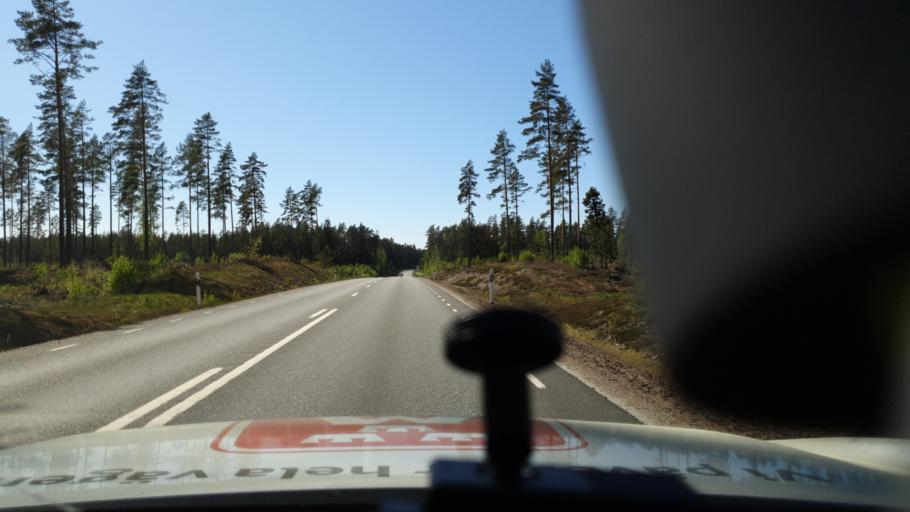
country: SE
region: Joenkoeping
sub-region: Vetlanda Kommun
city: Vetlanda
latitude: 57.4097
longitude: 15.2819
